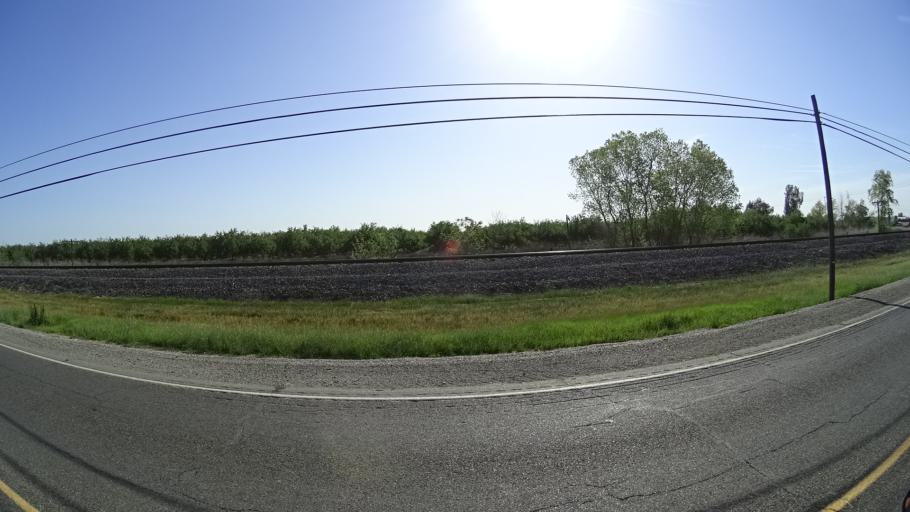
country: US
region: California
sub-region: Glenn County
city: Willows
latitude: 39.5401
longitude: -122.1935
